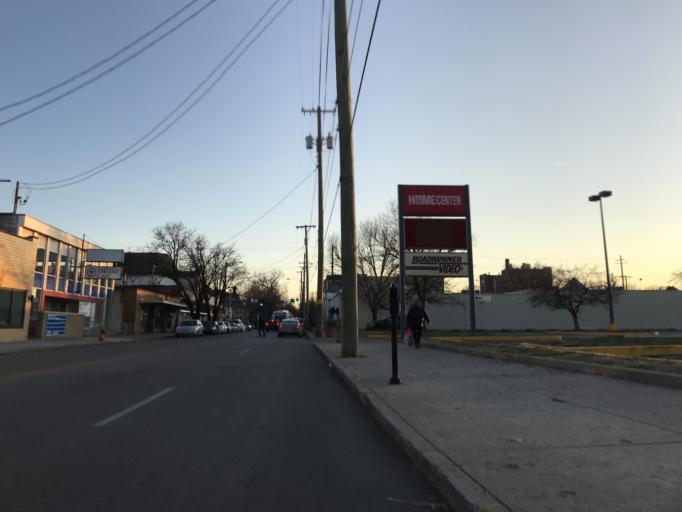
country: US
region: Kentucky
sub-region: Jefferson County
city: Louisville
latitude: 38.2360
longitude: -85.7602
